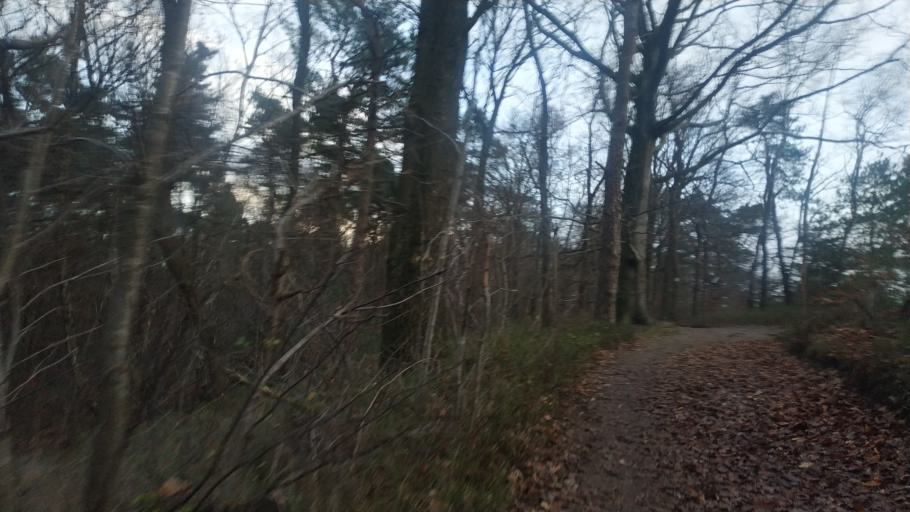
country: DE
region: North Rhine-Westphalia
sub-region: Regierungsbezirk Munster
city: Horstel
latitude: 52.2813
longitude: 7.5975
